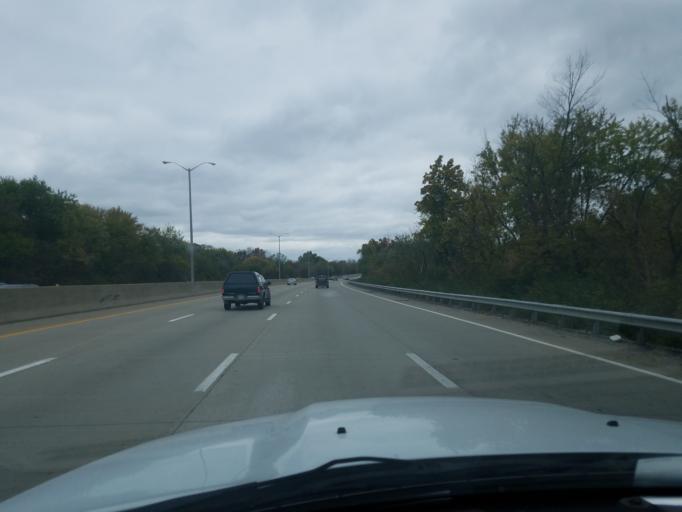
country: US
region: Kentucky
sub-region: Jefferson County
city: Shively
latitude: 38.2026
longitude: -85.8275
